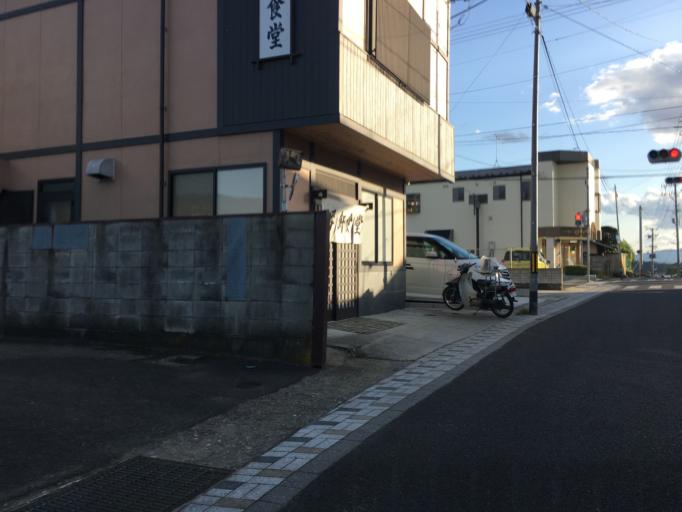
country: JP
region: Fukushima
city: Fukushima-shi
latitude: 37.8315
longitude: 140.4517
